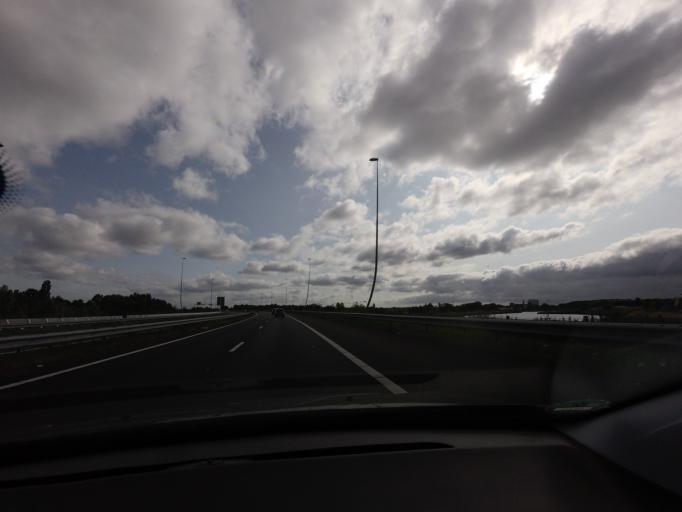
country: NL
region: North Holland
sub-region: Gemeente Zaanstad
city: Zaandam
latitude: 52.3890
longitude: 4.7698
